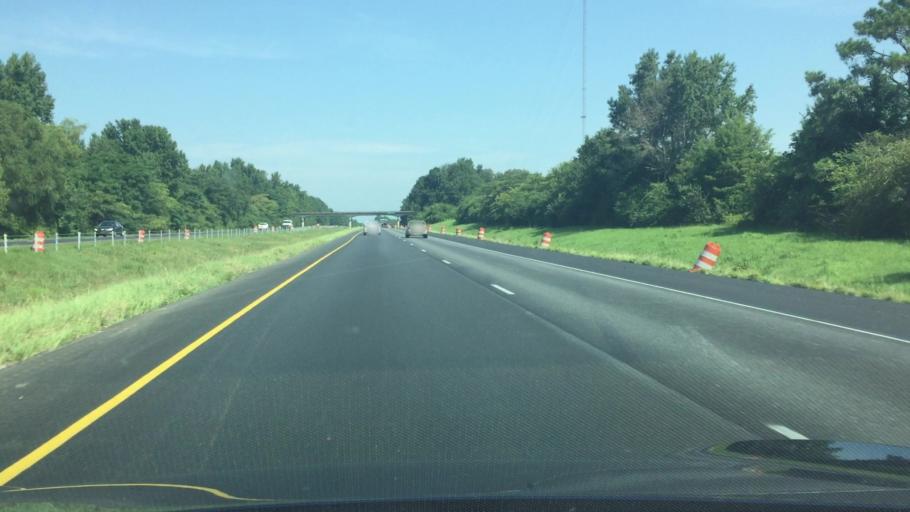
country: US
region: Alabama
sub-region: Autauga County
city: Marbury
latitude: 32.7588
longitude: -86.5580
